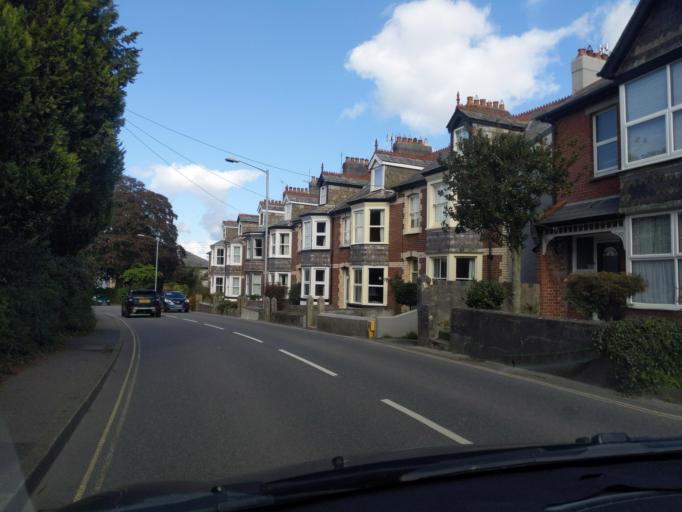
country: GB
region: England
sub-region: Cornwall
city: Launceston
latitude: 50.6327
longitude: -4.3529
